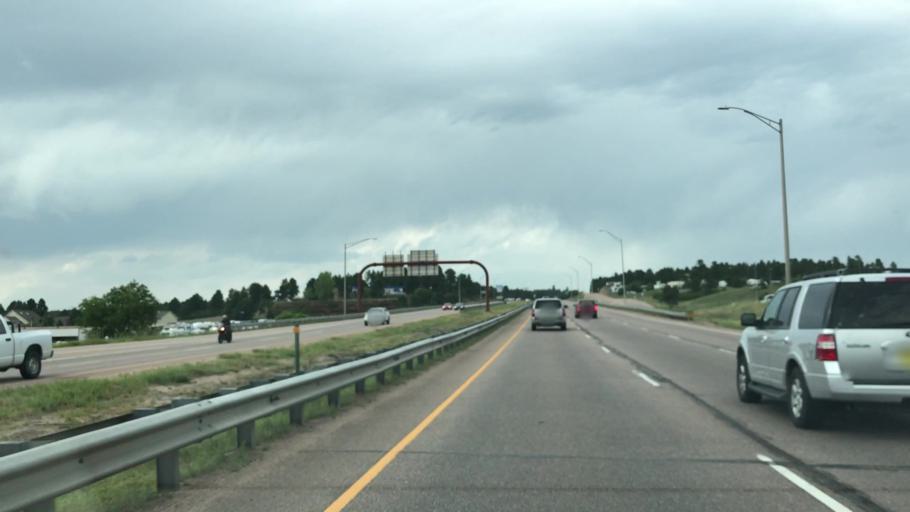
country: US
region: Colorado
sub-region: El Paso County
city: Woodmoor
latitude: 39.1096
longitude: -104.8650
